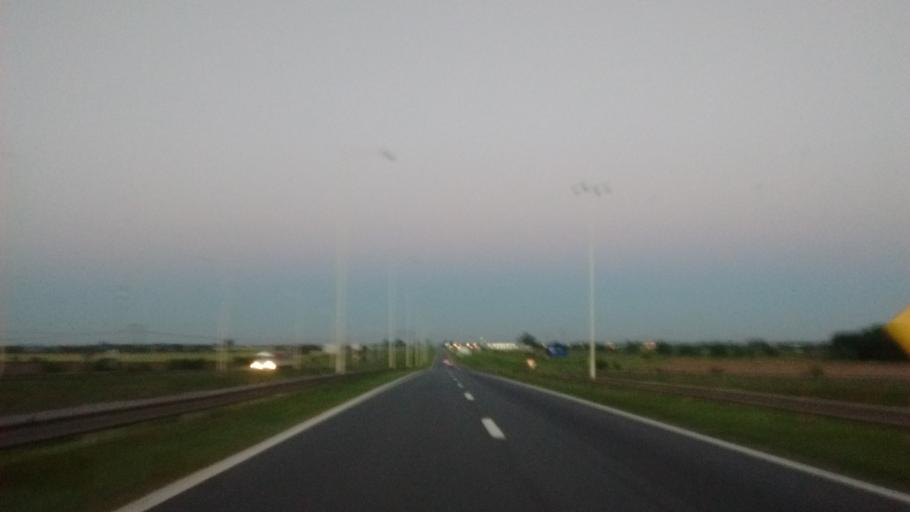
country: AR
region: Santa Fe
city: Roldan
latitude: -32.9264
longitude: -60.9014
